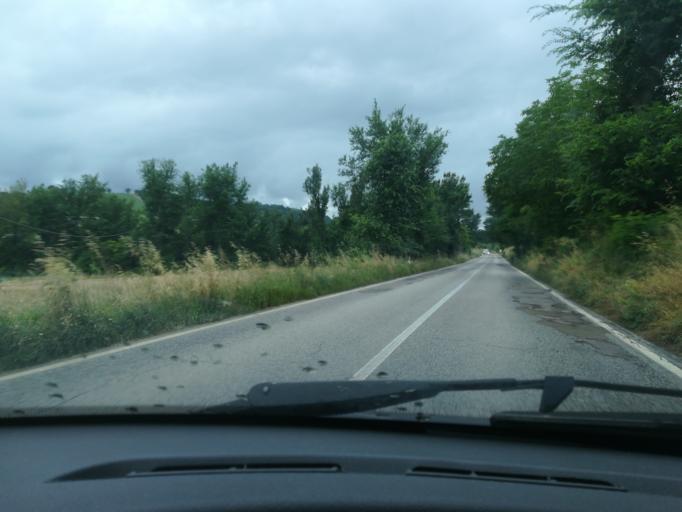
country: IT
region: The Marches
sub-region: Provincia di Macerata
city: San Ginesio
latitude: 43.1031
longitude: 13.3514
